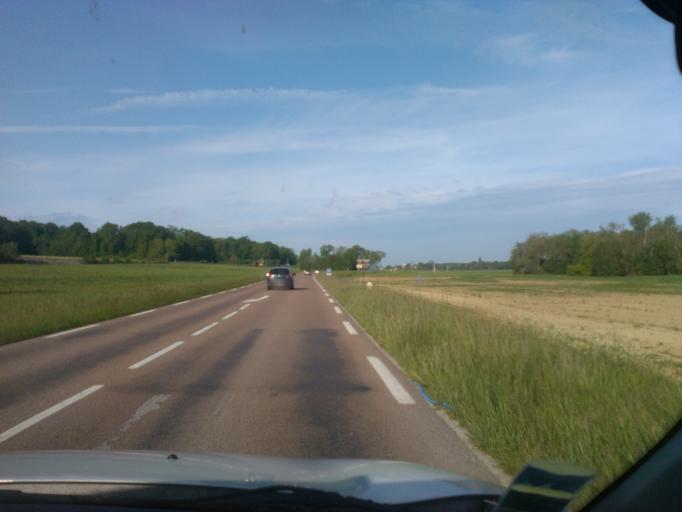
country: FR
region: Champagne-Ardenne
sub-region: Departement de l'Aube
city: Vendeuvre-sur-Barse
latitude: 48.2352
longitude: 4.4189
